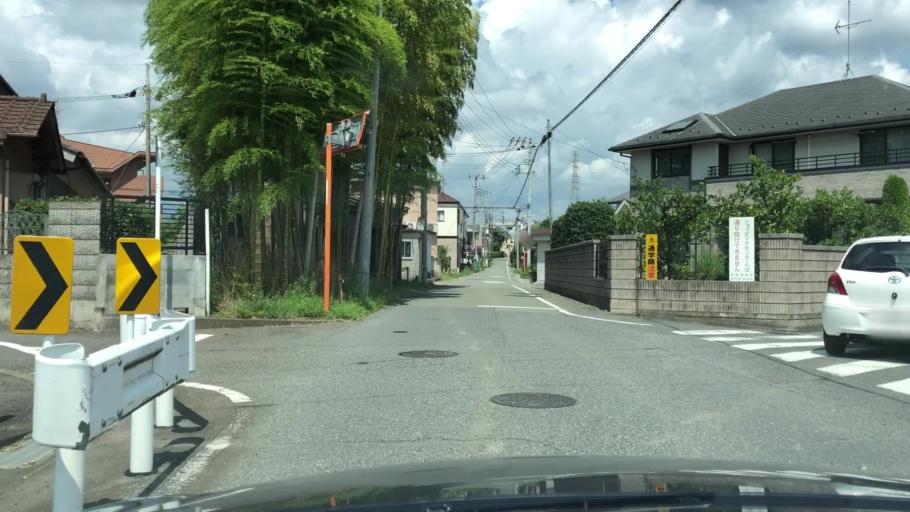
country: JP
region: Tokyo
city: Fussa
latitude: 35.7237
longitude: 139.2742
